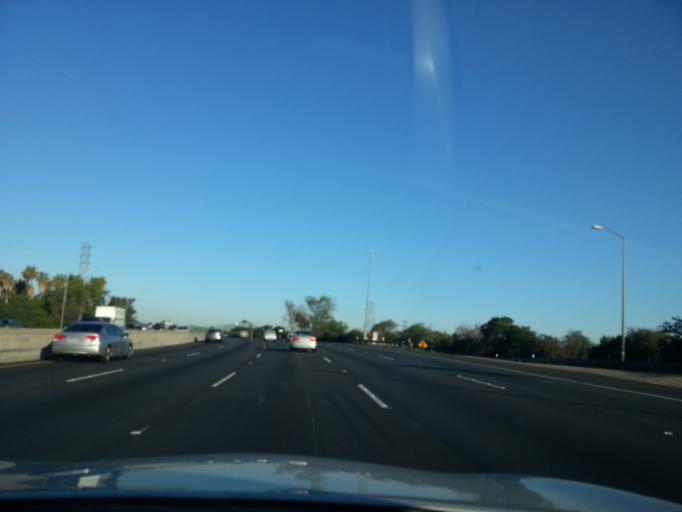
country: US
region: California
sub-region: Los Angeles County
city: Universal City
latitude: 34.1458
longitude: -118.3688
